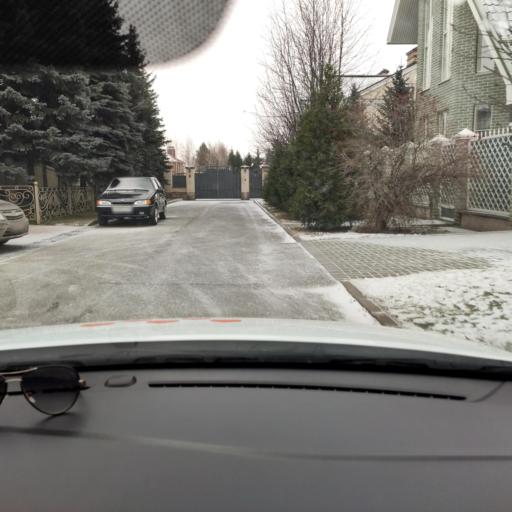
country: RU
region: Tatarstan
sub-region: Gorod Kazan'
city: Kazan
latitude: 55.8176
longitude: 49.2263
